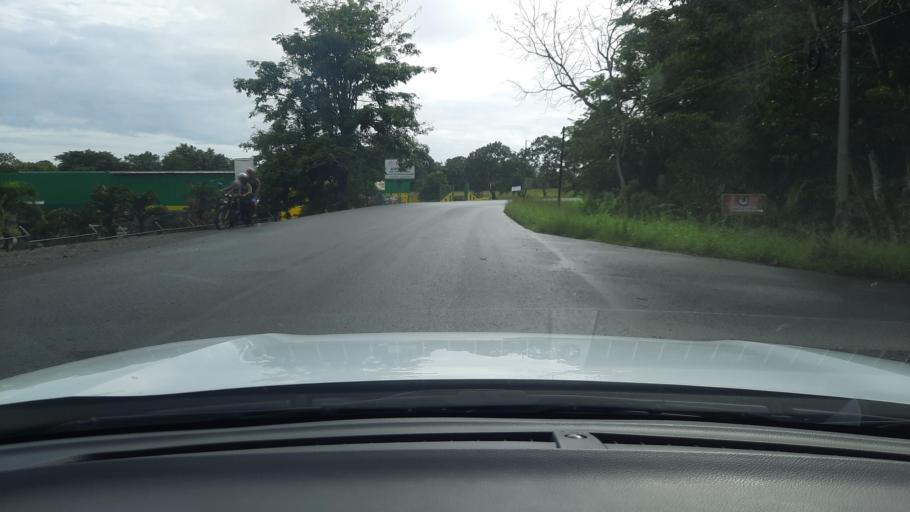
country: CR
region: Alajuela
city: San Jose
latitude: 10.9578
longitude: -85.1353
